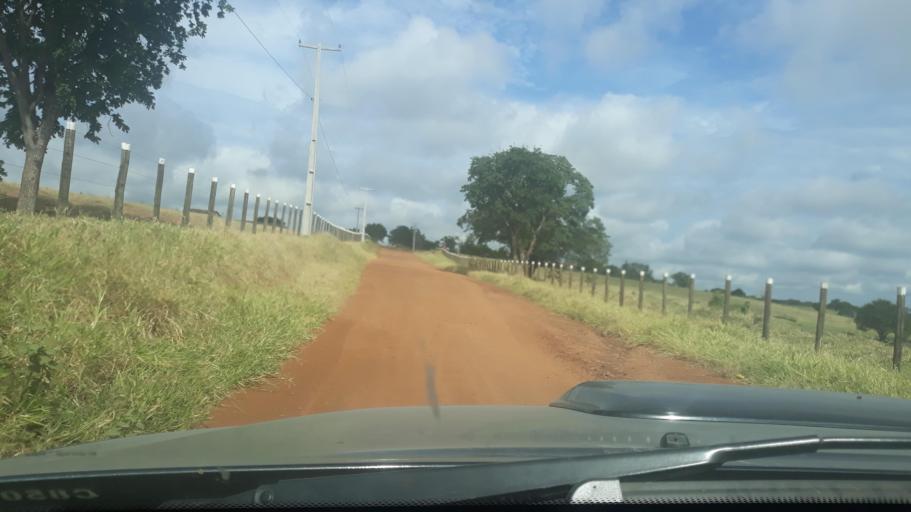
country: BR
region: Bahia
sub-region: Riacho De Santana
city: Riacho de Santana
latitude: -13.9005
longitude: -42.8837
